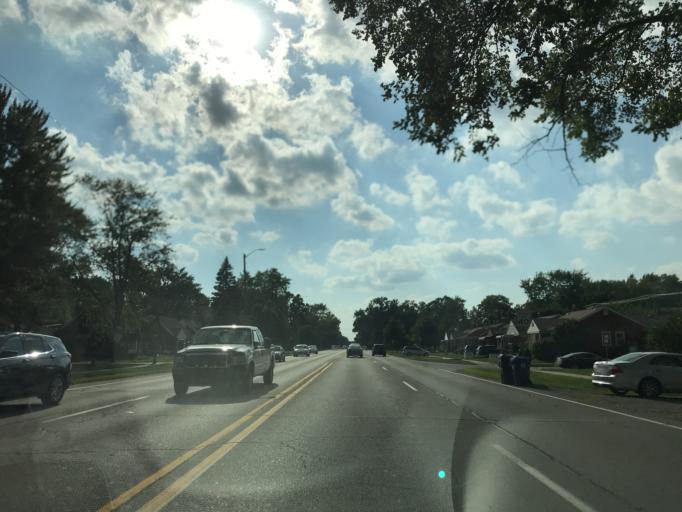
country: US
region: Michigan
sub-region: Wayne County
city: Redford
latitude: 42.3993
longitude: -83.3022
